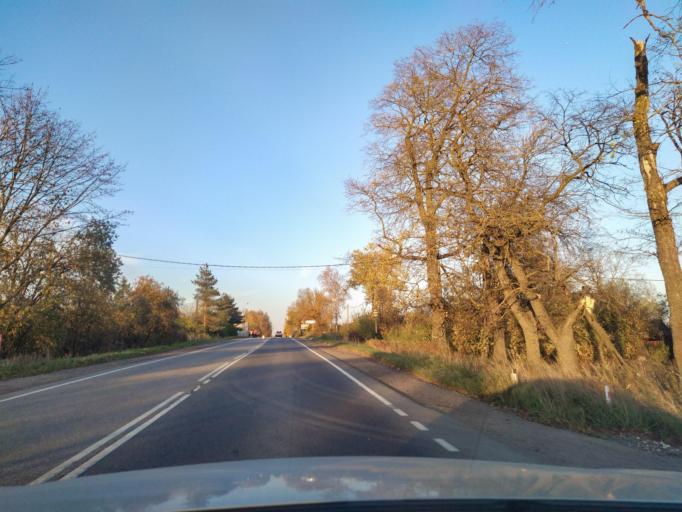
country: RU
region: Leningrad
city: Maloye Verevo
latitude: 59.6097
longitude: 30.1951
